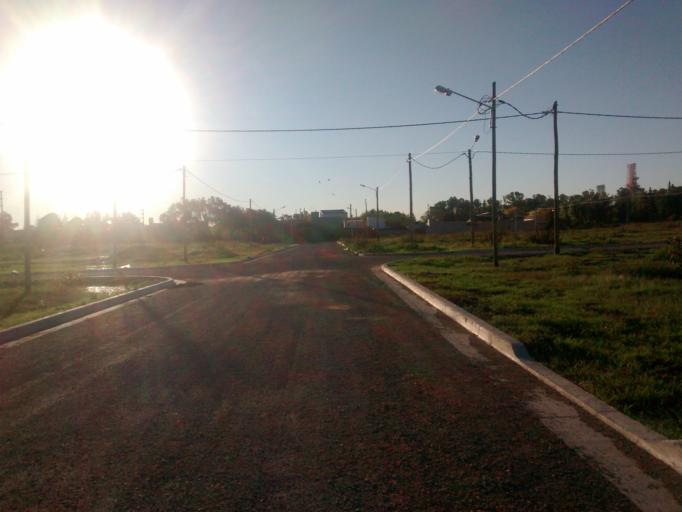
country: AR
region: Buenos Aires
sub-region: Partido de La Plata
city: La Plata
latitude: -34.9039
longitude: -57.9177
